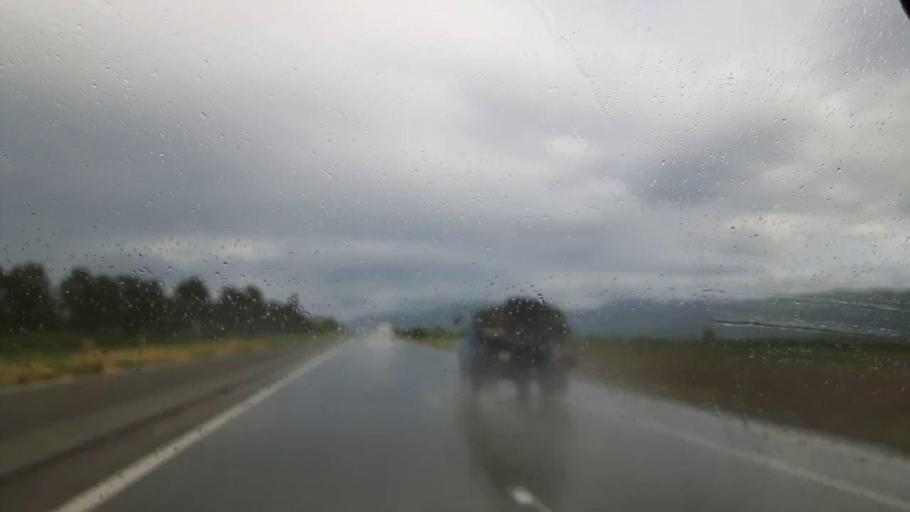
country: GE
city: Agara
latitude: 42.0409
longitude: 43.9294
